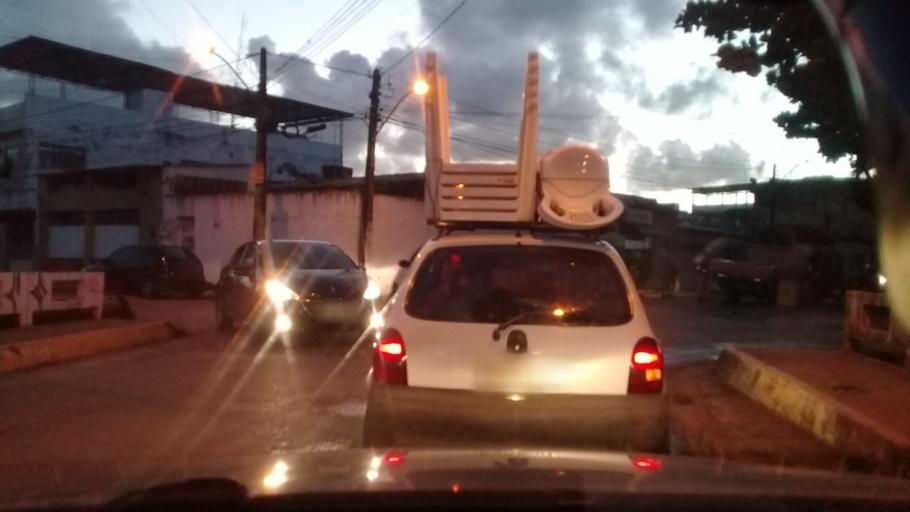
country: BR
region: Pernambuco
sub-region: Recife
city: Recife
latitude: -8.1153
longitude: -34.9162
